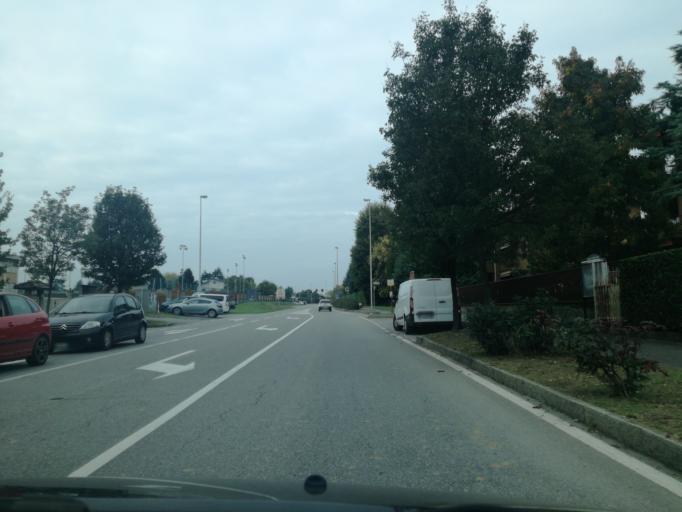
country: IT
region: Lombardy
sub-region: Provincia di Monza e Brianza
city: Bellusco
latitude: 45.6174
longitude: 9.4223
